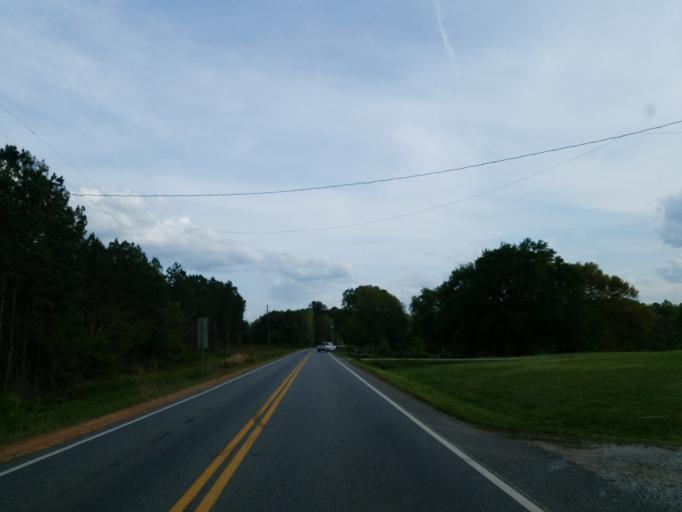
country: US
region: Georgia
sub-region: Cherokee County
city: Ball Ground
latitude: 34.3356
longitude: -84.2647
